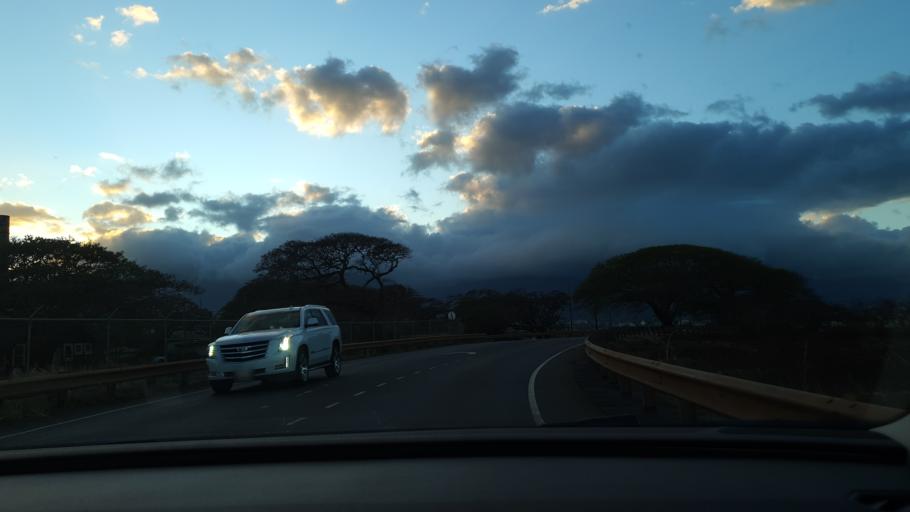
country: US
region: Hawaii
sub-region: Maui County
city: Kahului
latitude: 20.8692
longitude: -156.4515
